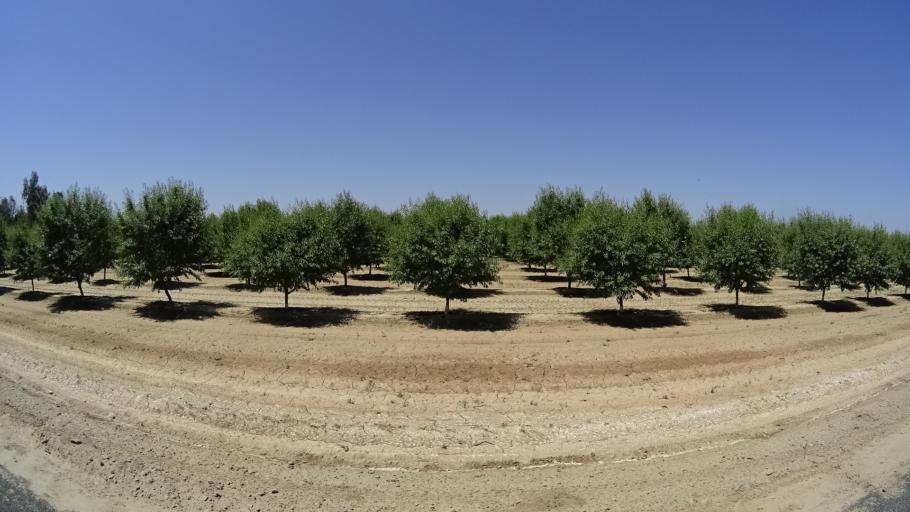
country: US
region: California
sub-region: Kings County
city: Armona
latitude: 36.2569
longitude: -119.7270
